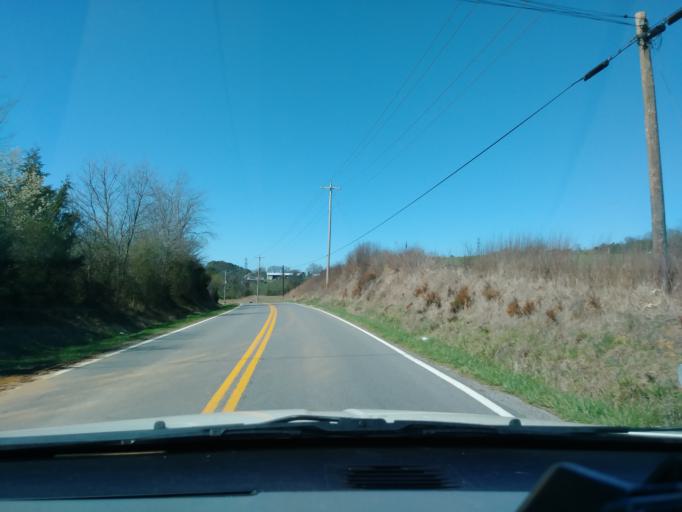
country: US
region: Tennessee
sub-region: Cocke County
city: Newport
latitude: 35.9971
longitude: -83.0765
